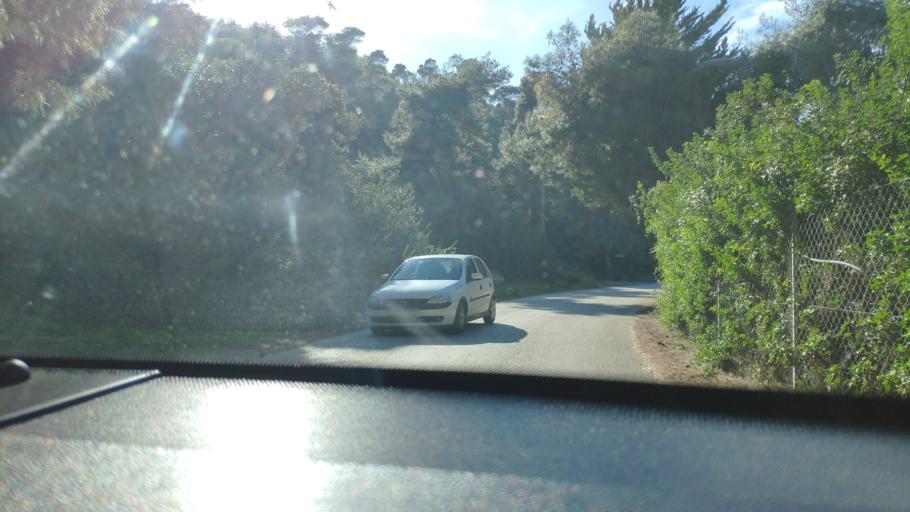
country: GR
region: Peloponnese
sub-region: Nomos Korinthias
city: Agioi Theodoroi
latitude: 38.0592
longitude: 23.1001
